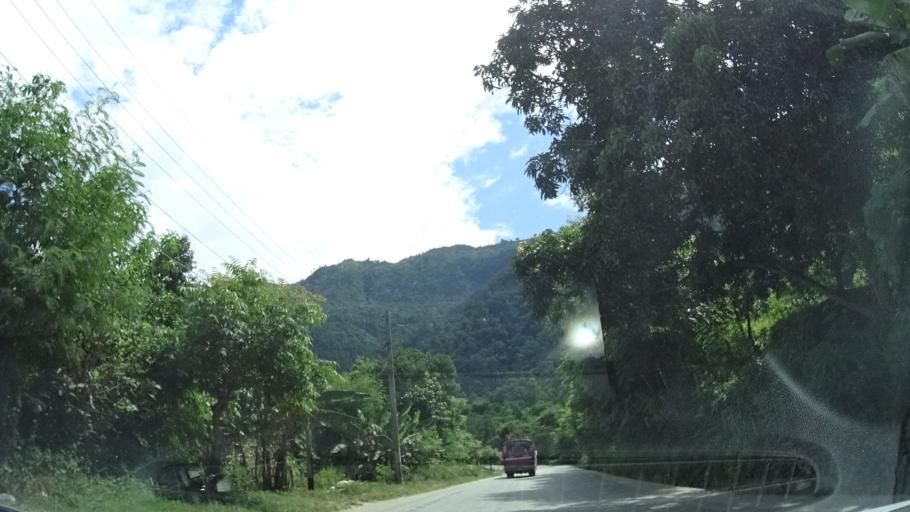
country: NP
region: Central Region
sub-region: Narayani Zone
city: Bharatpur
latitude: 27.8096
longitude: 84.7678
